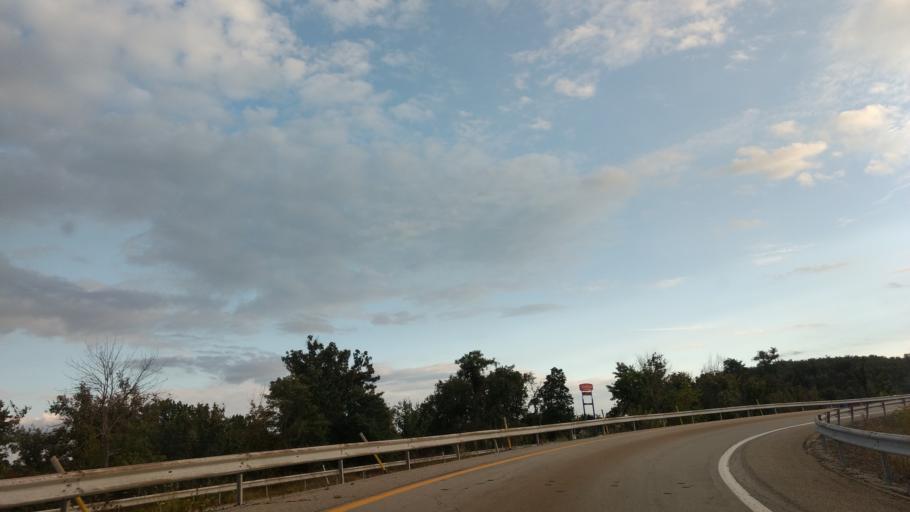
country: US
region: Pennsylvania
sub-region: Westmoreland County
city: West Newton
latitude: 40.1545
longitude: -79.7739
